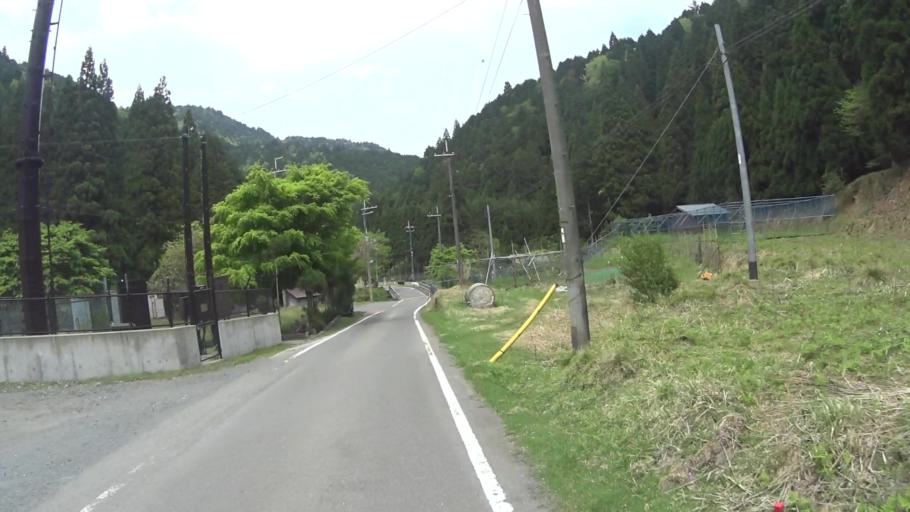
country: JP
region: Kyoto
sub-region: Kyoto-shi
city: Kamigyo-ku
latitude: 35.1874
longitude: 135.7339
